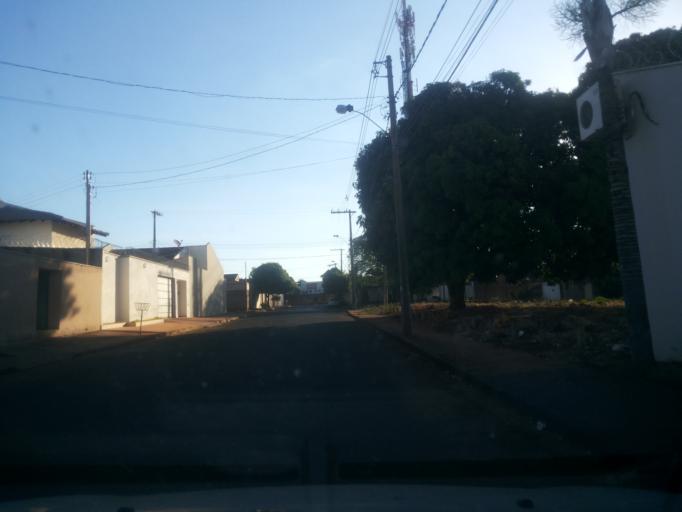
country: BR
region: Minas Gerais
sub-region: Ituiutaba
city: Ituiutaba
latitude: -18.9927
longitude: -49.4541
